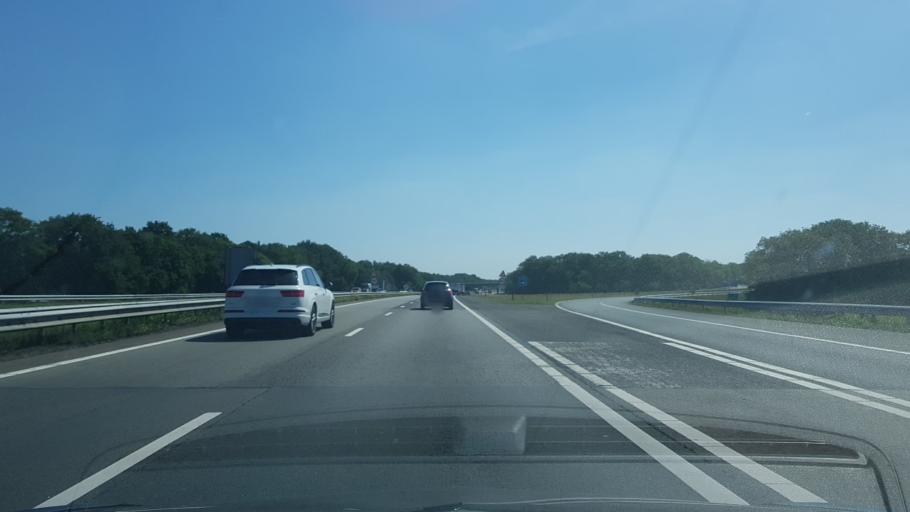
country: NL
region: Gelderland
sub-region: Gemeente Barneveld
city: Stroe
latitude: 52.1902
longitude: 5.6948
